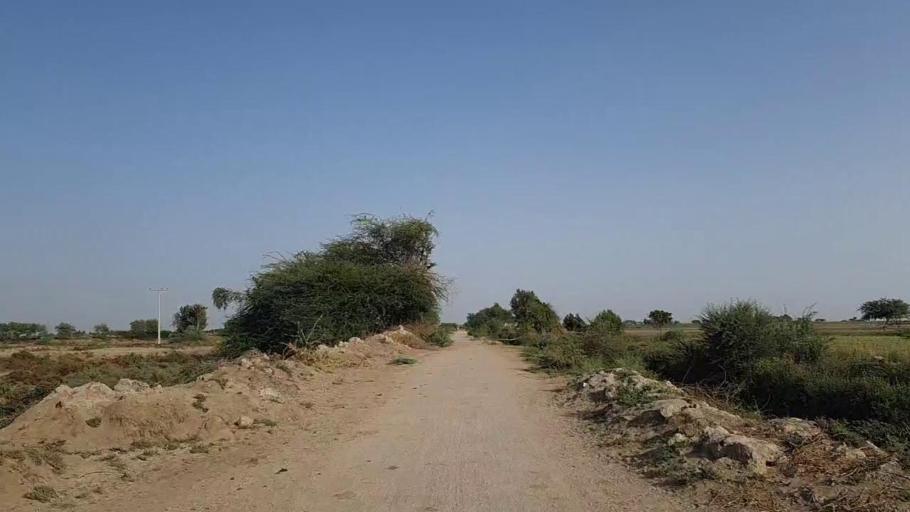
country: PK
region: Sindh
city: Jati
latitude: 24.2631
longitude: 68.1702
